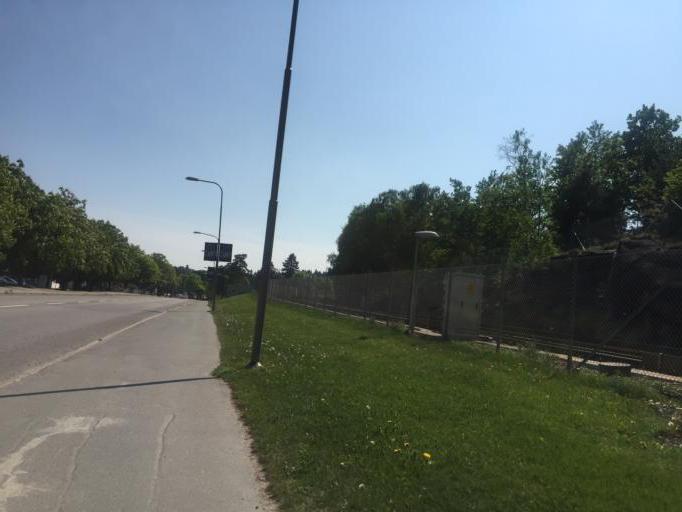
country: SE
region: Stockholm
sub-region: Stockholms Kommun
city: Arsta
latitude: 59.2802
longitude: 18.0692
